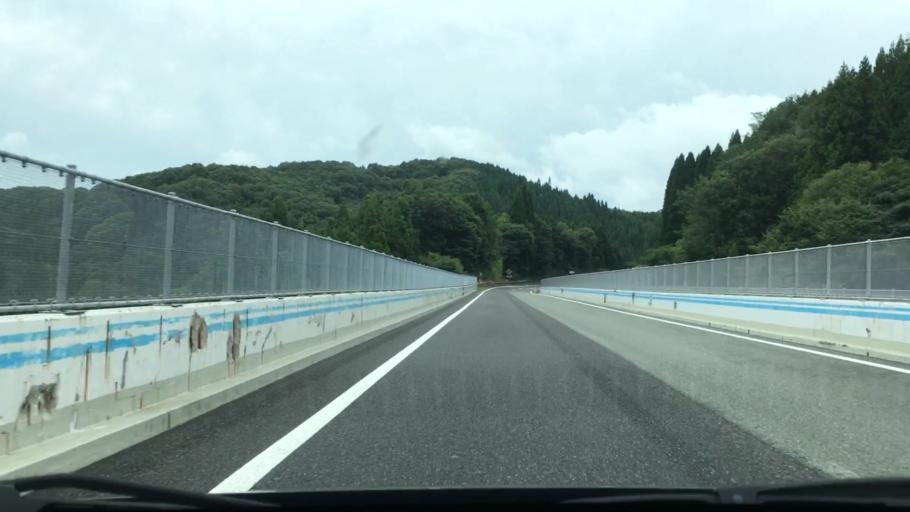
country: JP
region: Hiroshima
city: Shobara
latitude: 34.8814
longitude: 133.1920
